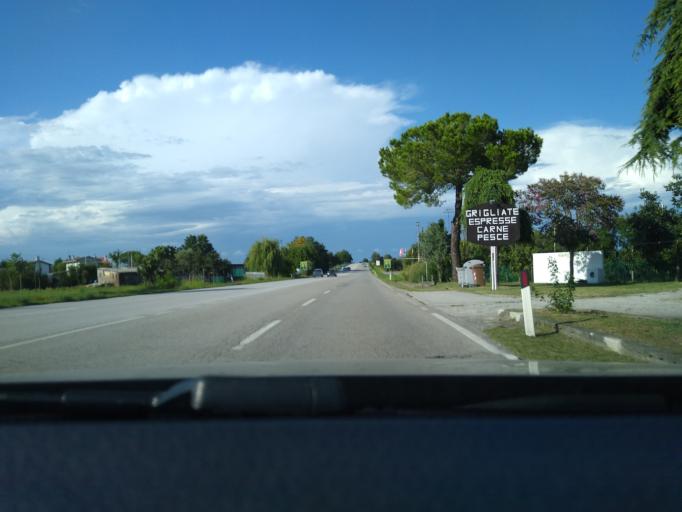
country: IT
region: Friuli Venezia Giulia
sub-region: Provincia di Udine
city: Latisana
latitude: 45.7848
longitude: 13.0223
